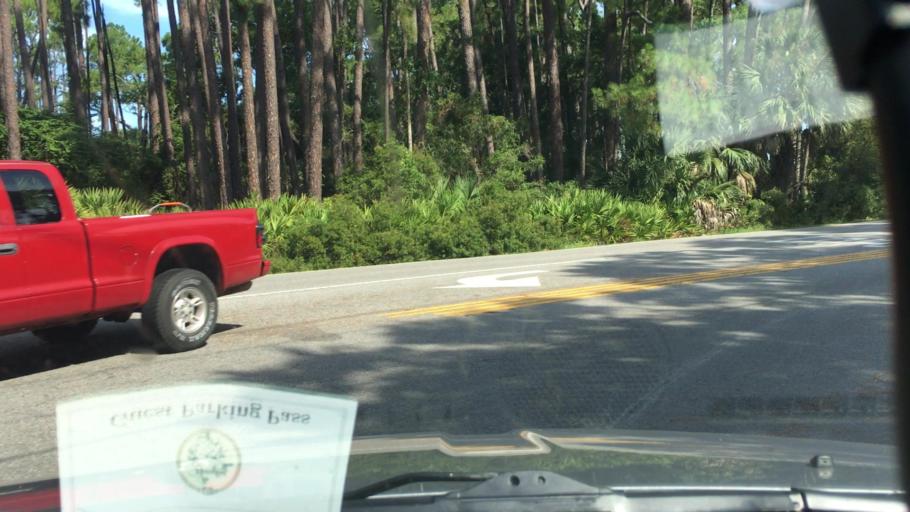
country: US
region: South Carolina
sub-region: Beaufort County
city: Beaufort
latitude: 32.3738
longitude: -80.4465
